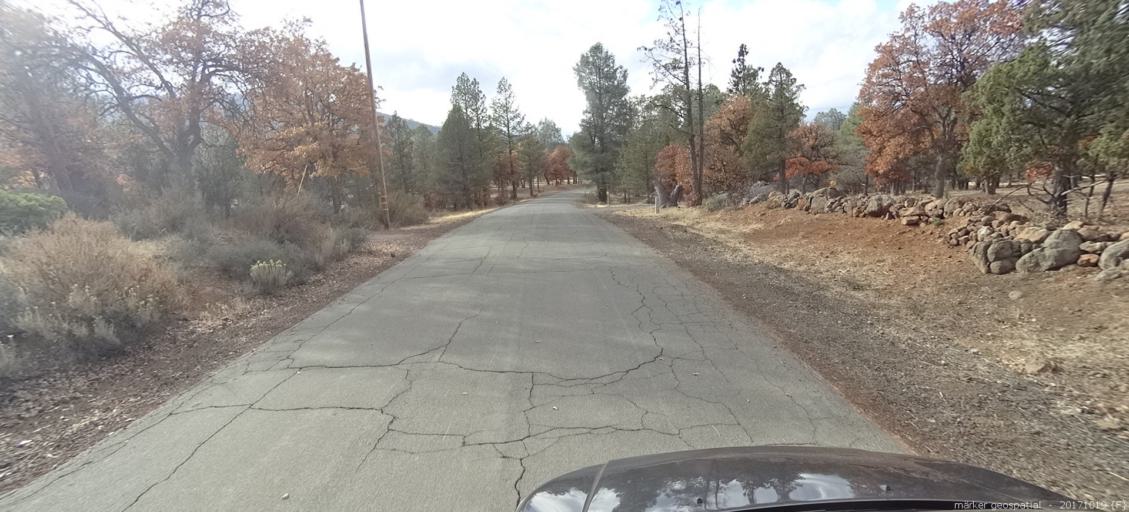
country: US
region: California
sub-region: Shasta County
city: Burney
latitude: 40.9715
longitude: -121.4418
